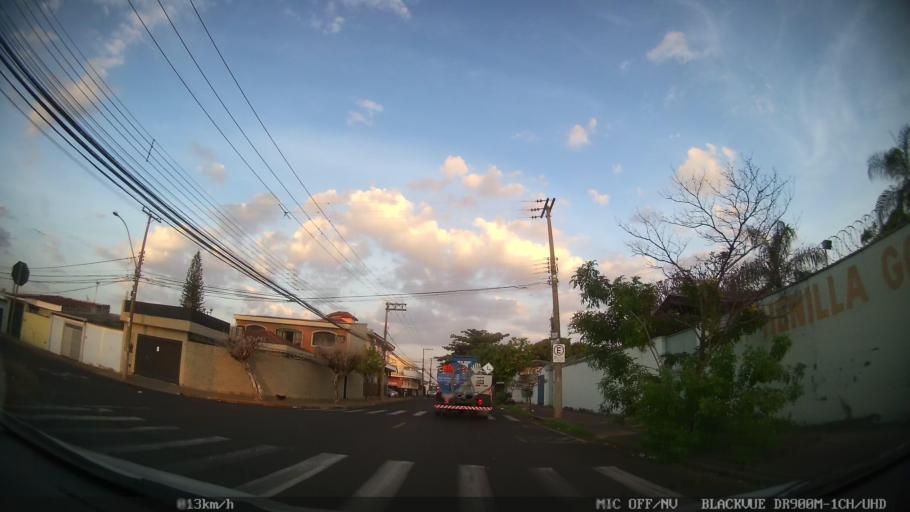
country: BR
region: Sao Paulo
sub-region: Ribeirao Preto
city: Ribeirao Preto
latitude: -21.1254
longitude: -47.8140
